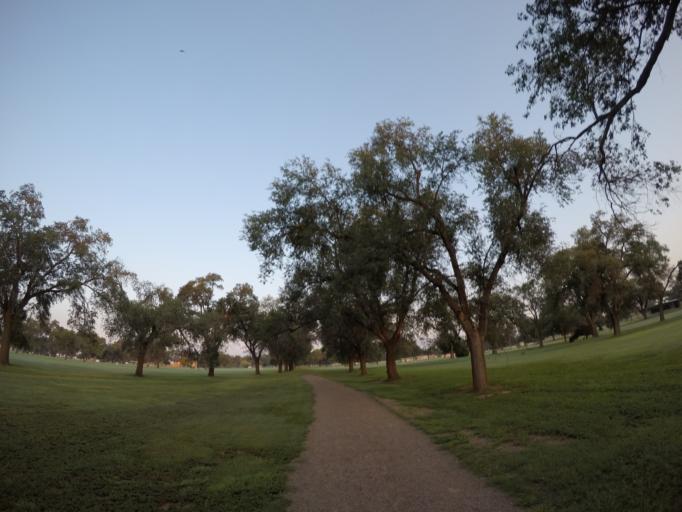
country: US
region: New Mexico
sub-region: Curry County
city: Clovis
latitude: 34.4067
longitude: -103.1809
